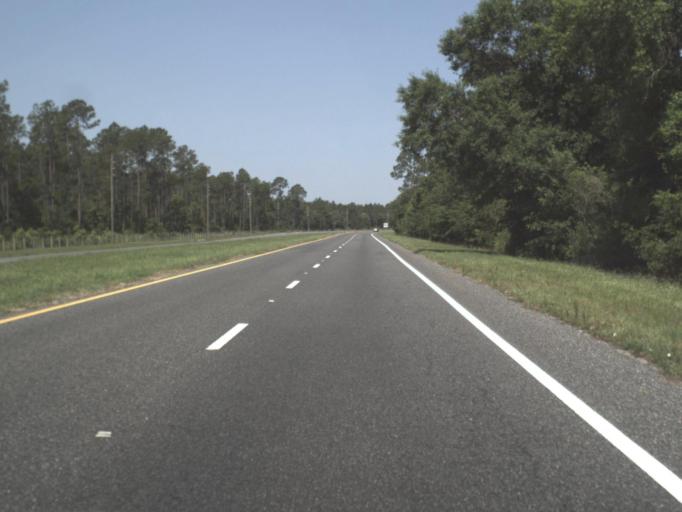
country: US
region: Florida
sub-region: Clay County
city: Middleburg
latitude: 29.9784
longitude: -81.9216
